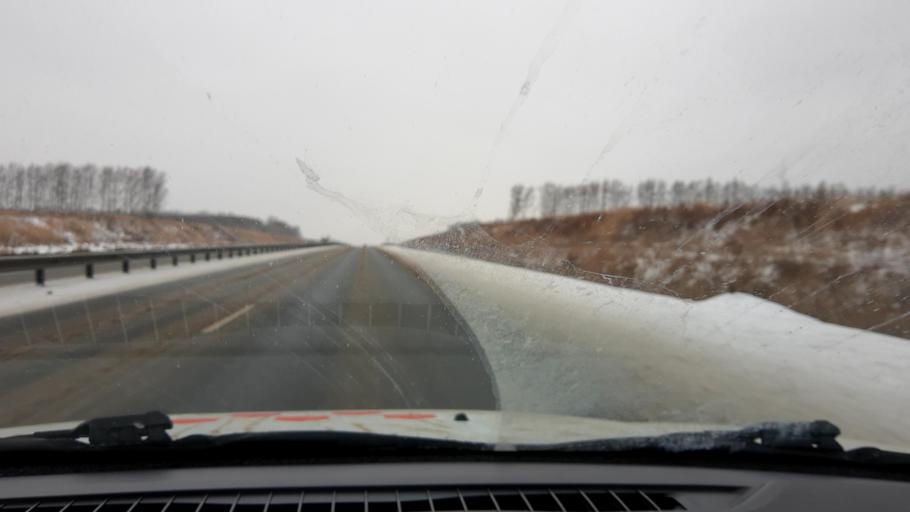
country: RU
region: Nizjnij Novgorod
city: Afonino
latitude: 56.1034
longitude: 44.0101
